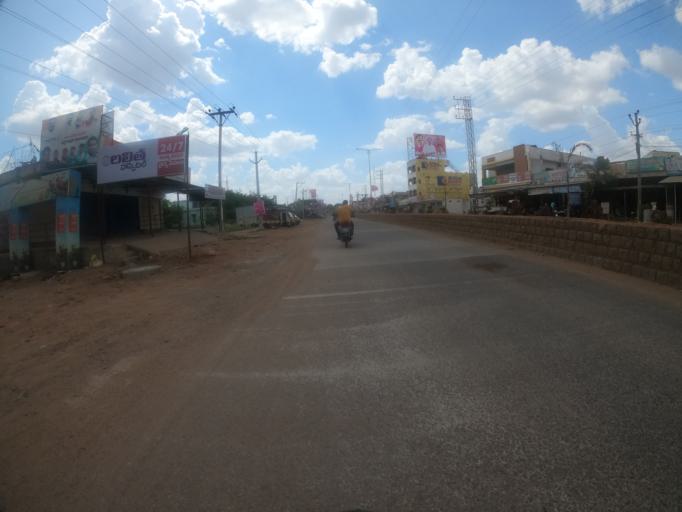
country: IN
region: Telangana
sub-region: Rangareddi
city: Sriramnagar
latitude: 17.3106
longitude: 78.1414
